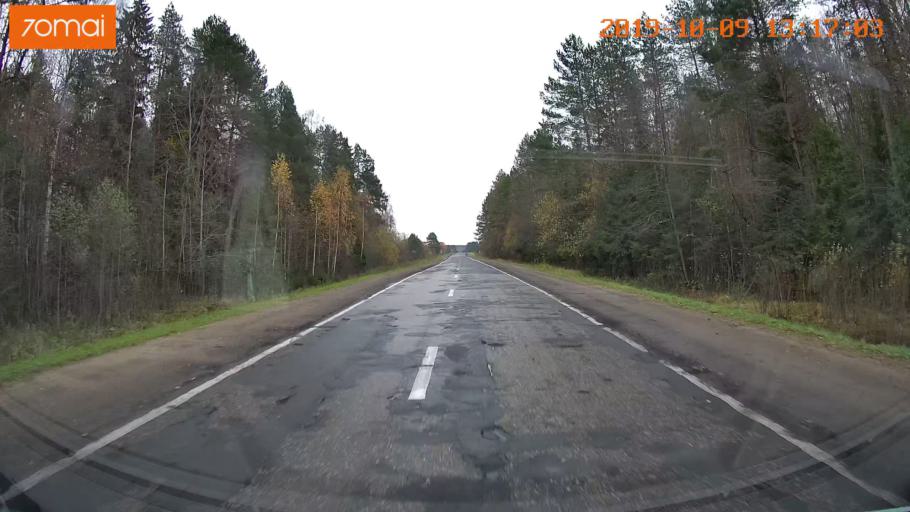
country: RU
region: Jaroslavl
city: Lyubim
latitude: 58.3568
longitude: 40.7746
